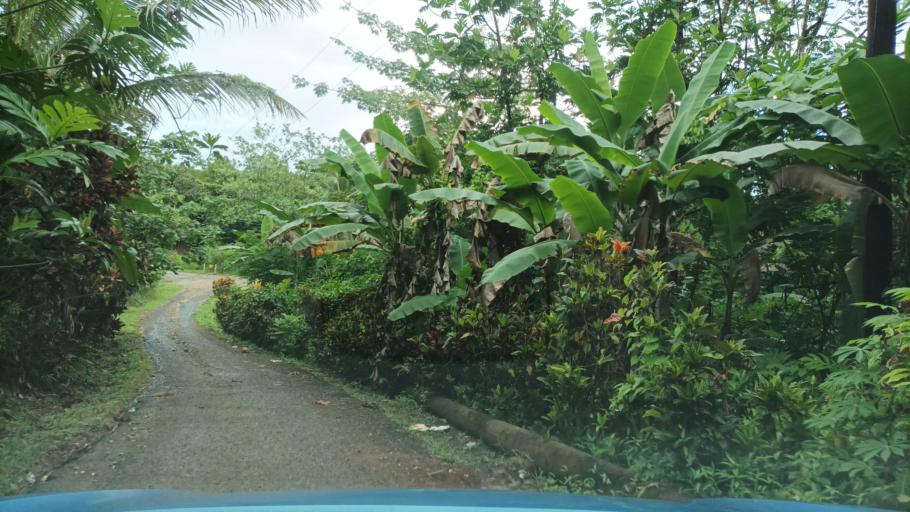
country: FM
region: Pohnpei
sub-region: Sokehs Municipality
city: Palikir - National Government Center
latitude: 6.8305
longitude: 158.1572
